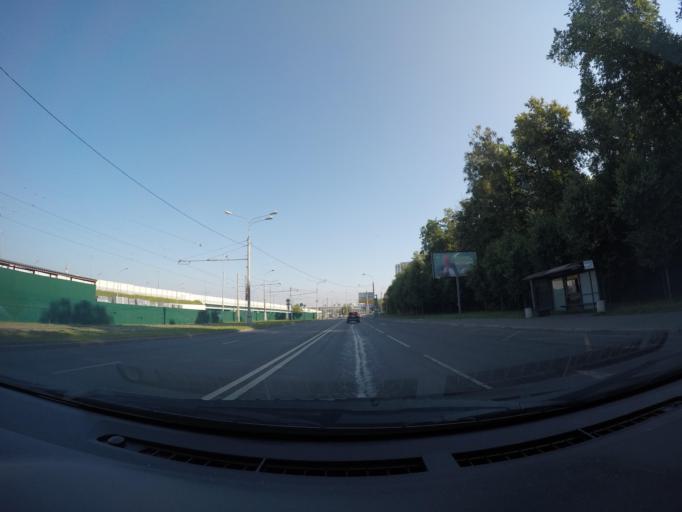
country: RU
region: Moskovskaya
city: Bogorodskoye
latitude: 55.7848
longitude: 37.7460
